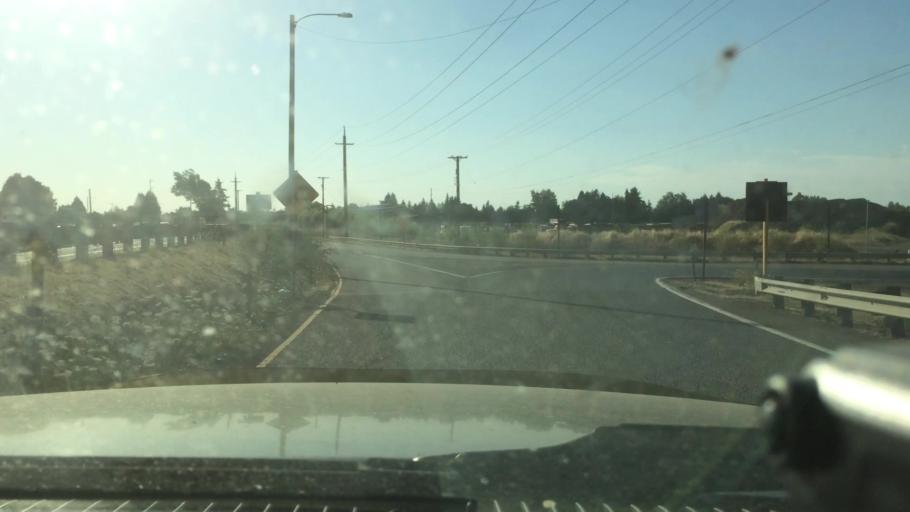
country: US
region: Oregon
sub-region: Lane County
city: Eugene
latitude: 44.0971
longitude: -123.1099
